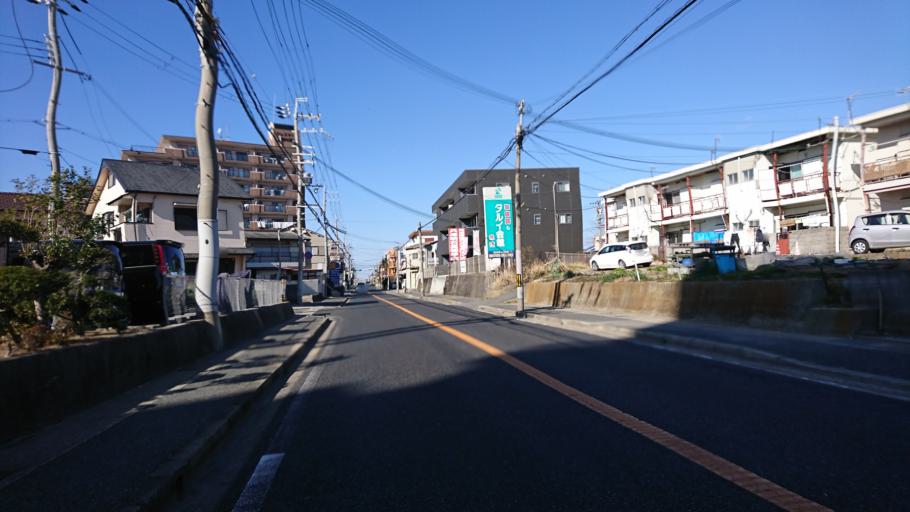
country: JP
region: Hyogo
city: Akashi
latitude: 34.6624
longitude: 134.9484
